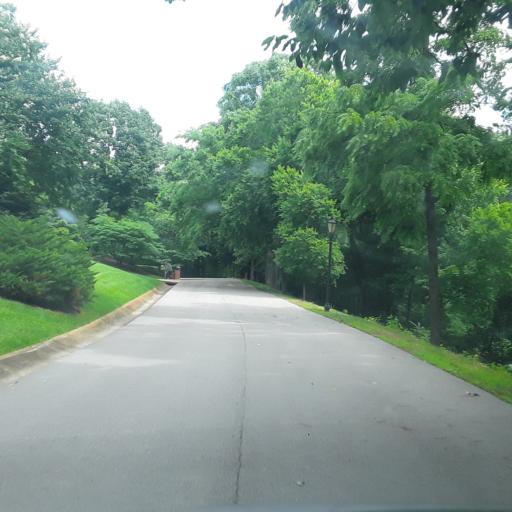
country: US
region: Tennessee
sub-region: Davidson County
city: Oak Hill
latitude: 36.0686
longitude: -86.7823
